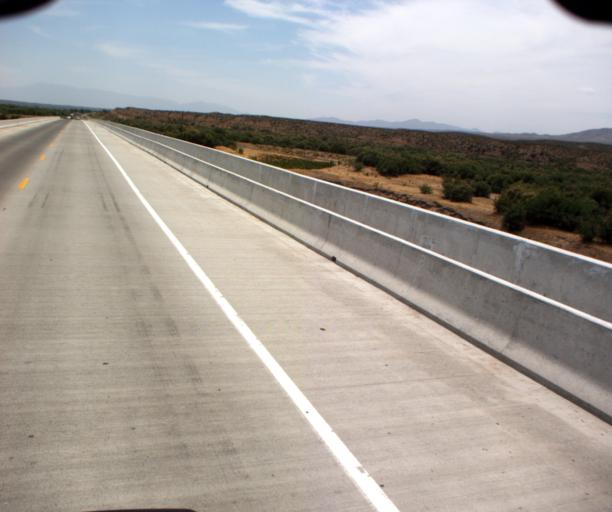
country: US
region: Arizona
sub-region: Graham County
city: Bylas
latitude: 33.1652
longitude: -110.1342
